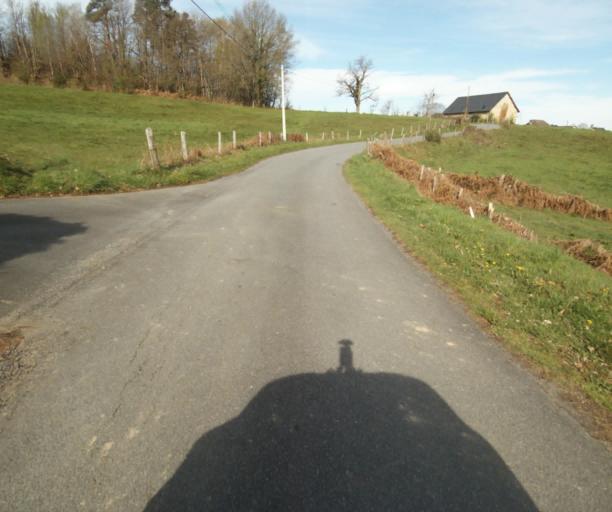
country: FR
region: Limousin
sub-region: Departement de la Correze
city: Correze
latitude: 45.3394
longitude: 1.8337
